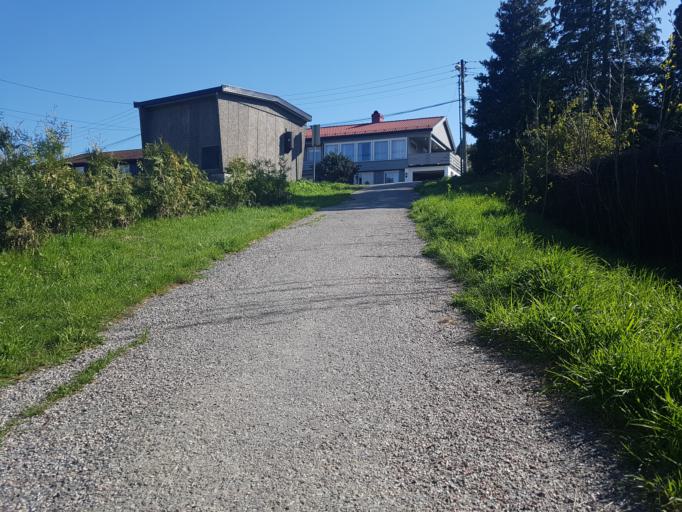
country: NO
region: Buskerud
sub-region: Drammen
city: Drammen
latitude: 59.7230
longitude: 10.2103
